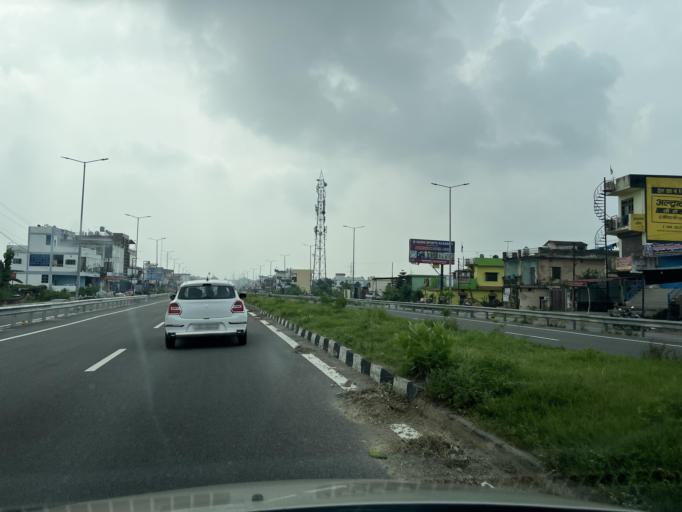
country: IN
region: Uttarakhand
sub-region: Dehradun
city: Raiwala
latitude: 30.0772
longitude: 78.1957
